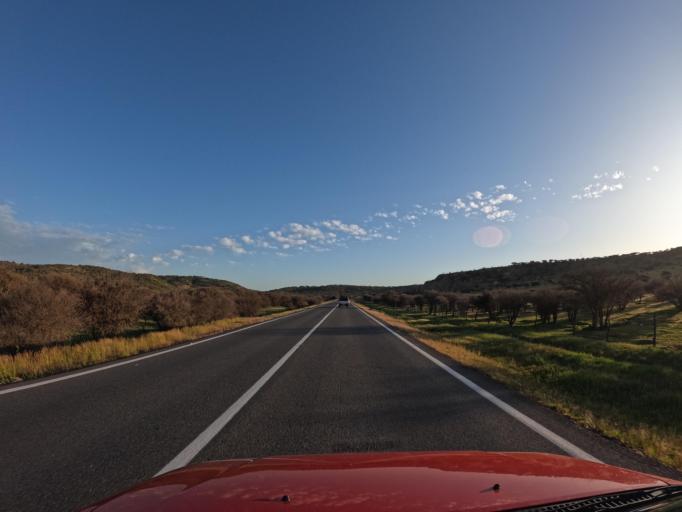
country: CL
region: O'Higgins
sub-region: Provincia de Colchagua
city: Santa Cruz
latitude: -34.3087
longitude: -71.7372
